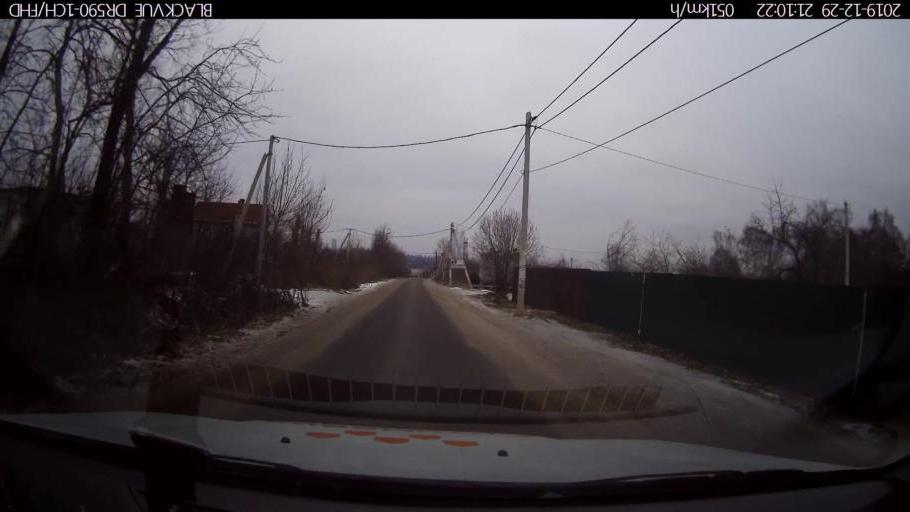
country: RU
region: Nizjnij Novgorod
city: Afonino
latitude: 56.2223
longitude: 44.0388
